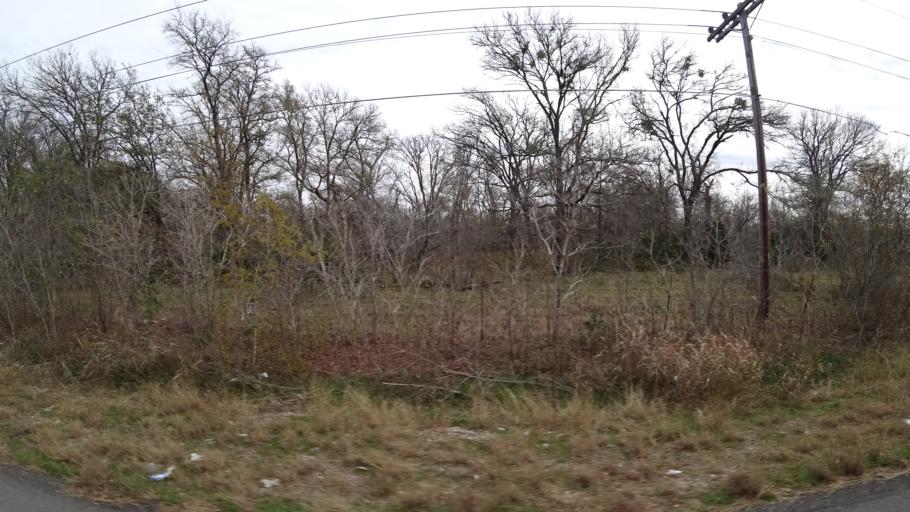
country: US
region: Texas
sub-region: Travis County
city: Garfield
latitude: 30.1474
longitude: -97.5634
